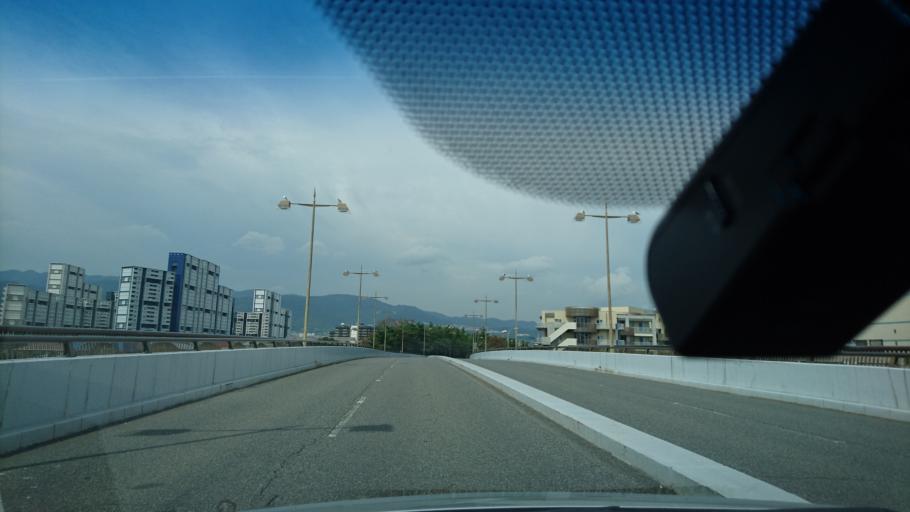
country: JP
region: Hyogo
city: Nishinomiya-hama
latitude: 34.7165
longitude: 135.3211
